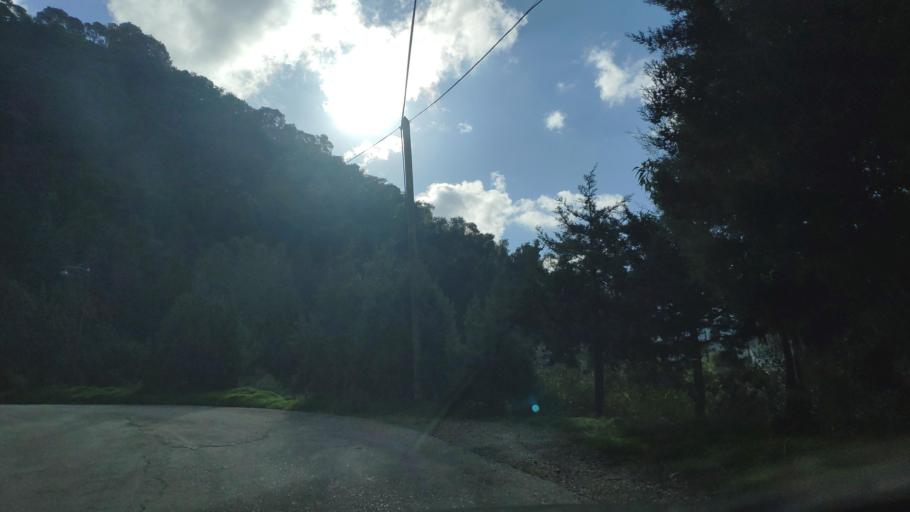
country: GR
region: West Greece
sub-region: Nomos Achaias
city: Aiyira
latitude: 38.1224
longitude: 22.4356
